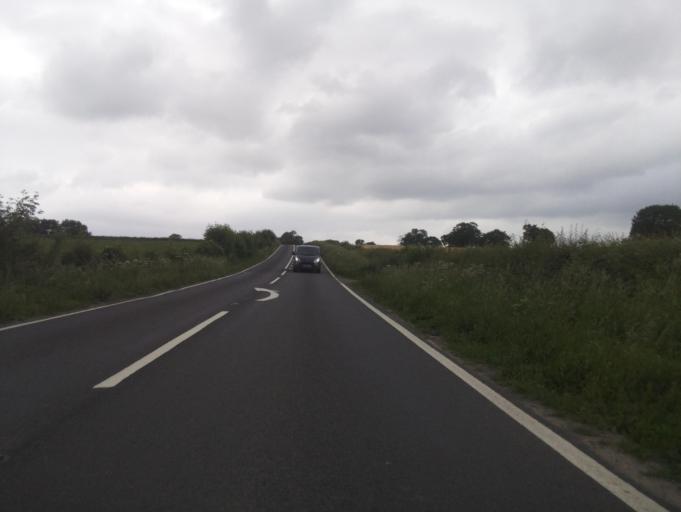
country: GB
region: England
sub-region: Staffordshire
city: Mayfield
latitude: 52.9564
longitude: -1.7584
